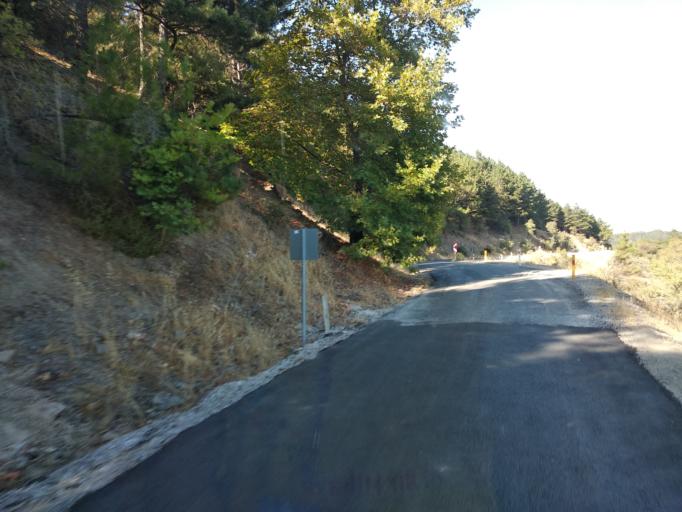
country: TR
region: Izmir
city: Gaziemir
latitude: 38.3167
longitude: 27.0095
